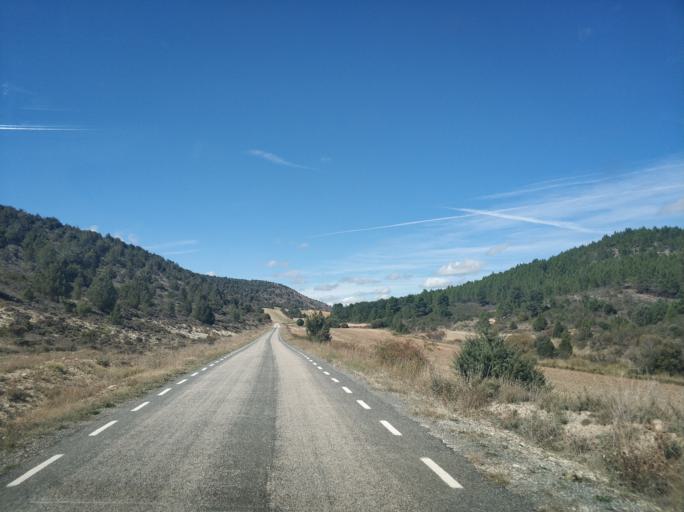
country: ES
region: Castille and Leon
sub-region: Provincia de Soria
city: Espeja de San Marcelino
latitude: 41.8148
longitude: -3.2307
